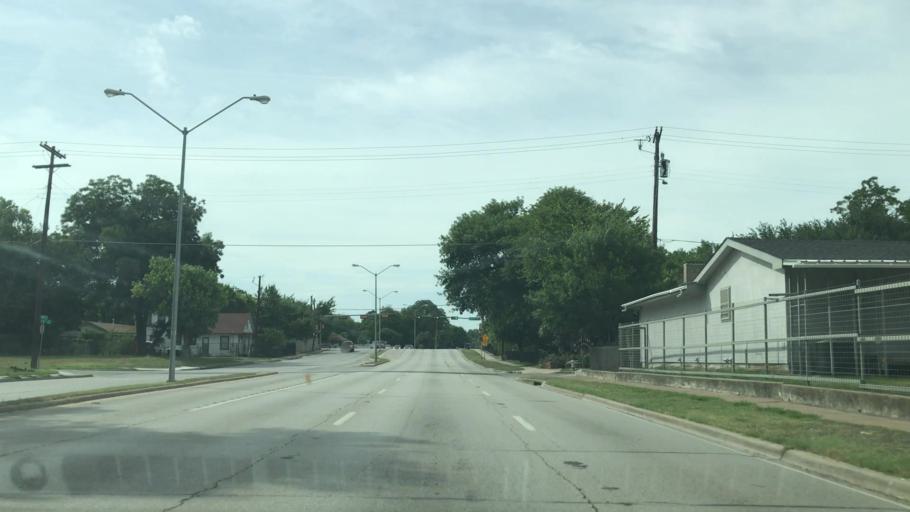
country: US
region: Texas
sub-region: Dallas County
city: Dallas
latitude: 32.7934
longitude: -96.7587
